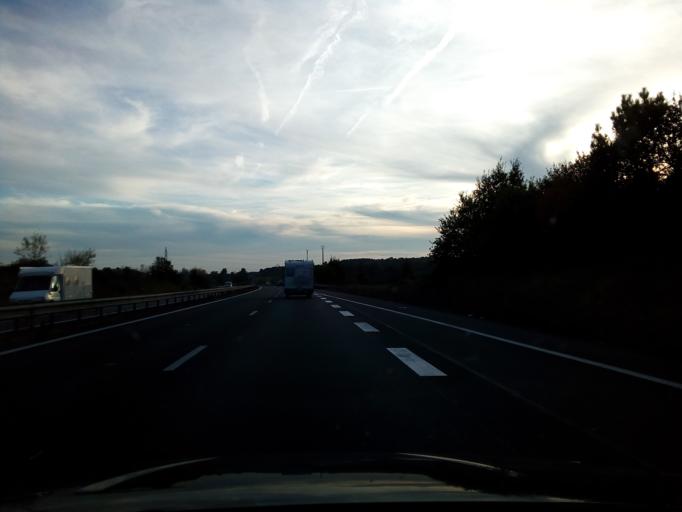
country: FR
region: Poitou-Charentes
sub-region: Departement de la Charente-Maritime
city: Montlieu-la-Garde
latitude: 45.2392
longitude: -0.2746
